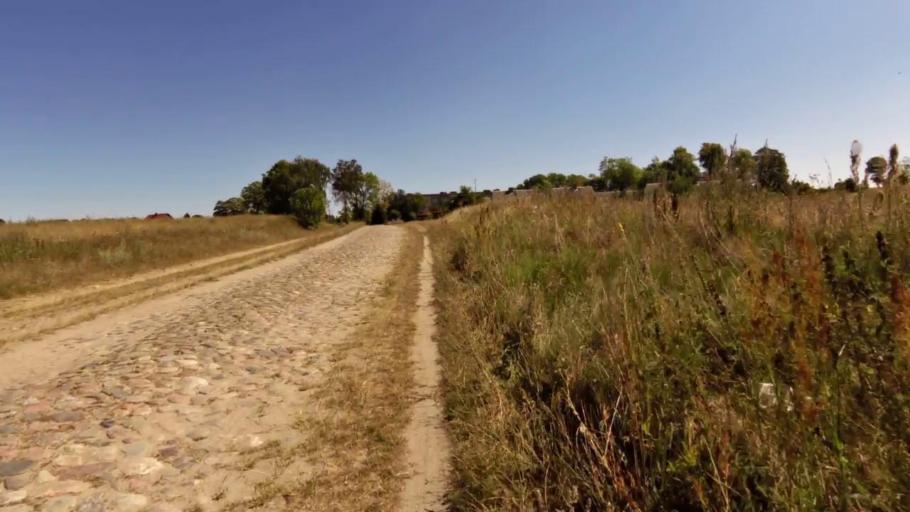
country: PL
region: West Pomeranian Voivodeship
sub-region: Powiat szczecinecki
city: Szczecinek
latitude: 53.6296
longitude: 16.6748
